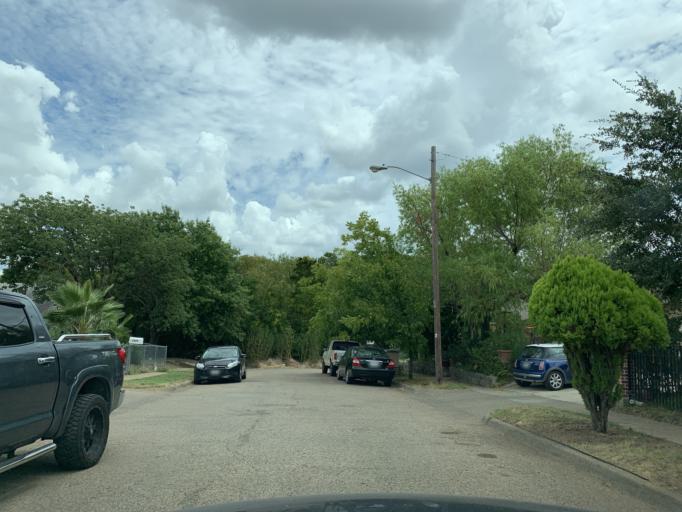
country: US
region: Texas
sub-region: Dallas County
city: Cockrell Hill
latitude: 32.7461
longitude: -96.8790
